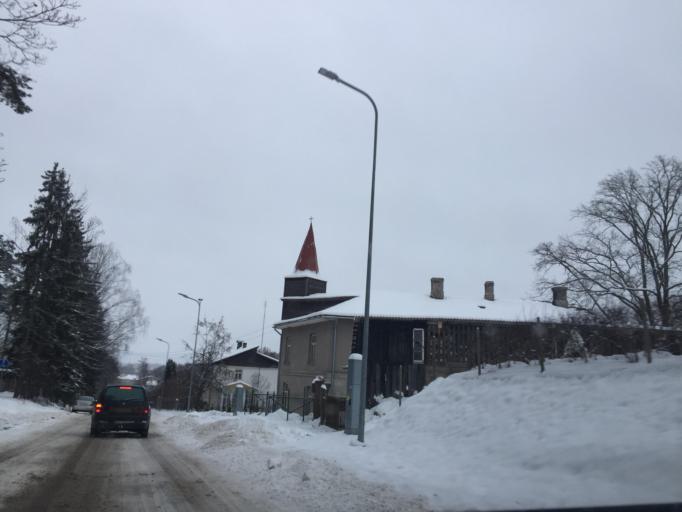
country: LV
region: Smiltene
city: Smiltene
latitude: 57.4234
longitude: 25.8975
